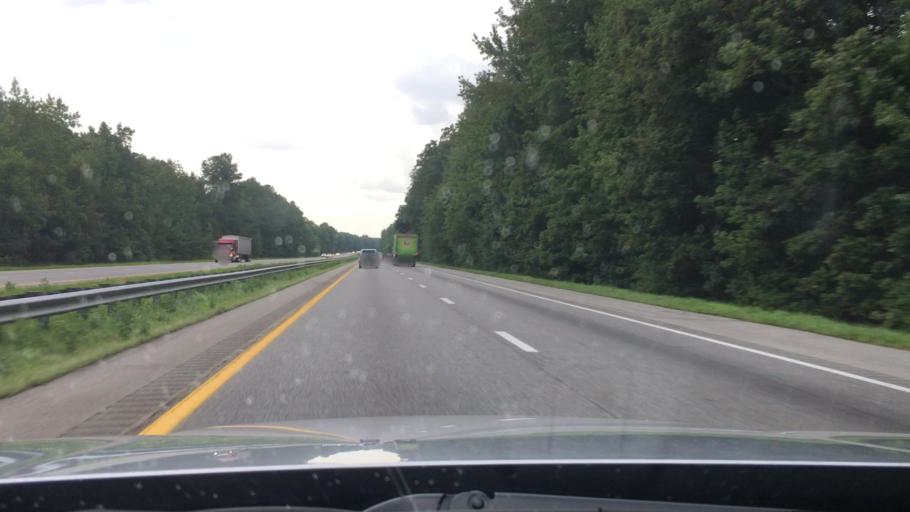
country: US
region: Virginia
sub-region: City of Emporia
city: Emporia
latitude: 36.5859
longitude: -77.5648
